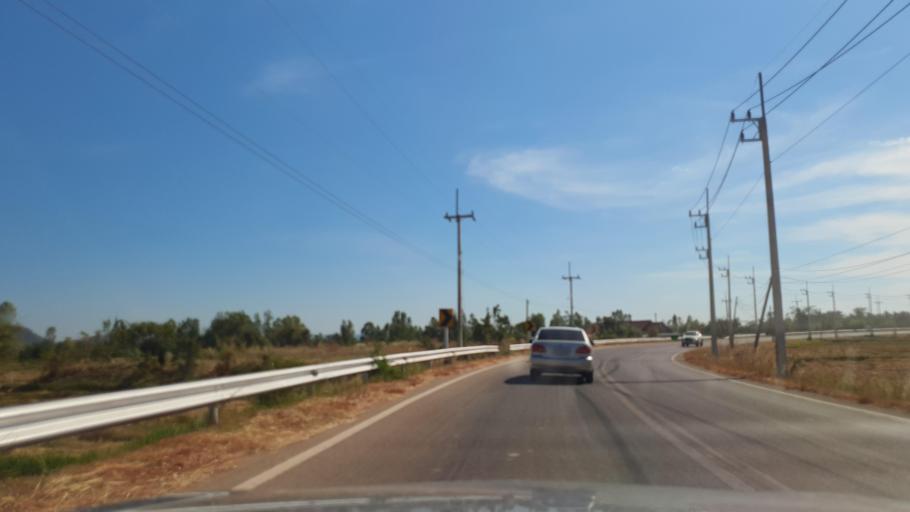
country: TH
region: Kalasin
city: Khao Wong
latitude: 16.7440
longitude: 104.1091
